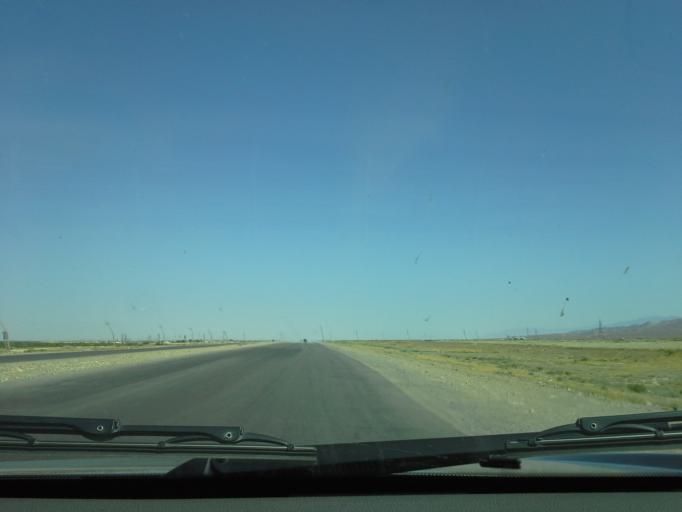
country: TM
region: Balkan
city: Serdar
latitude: 38.9553
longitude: 56.3816
